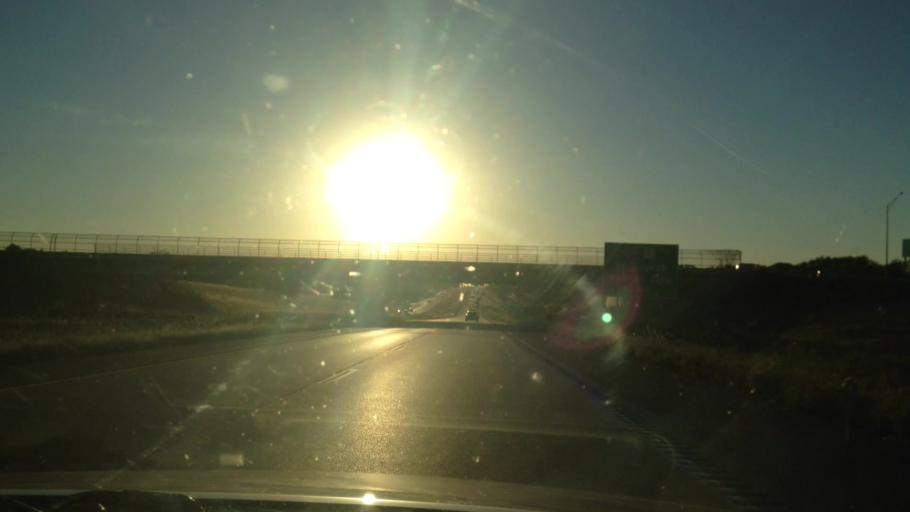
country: US
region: Missouri
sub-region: Platte County
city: Weatherby Lake
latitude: 39.2545
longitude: -94.6287
